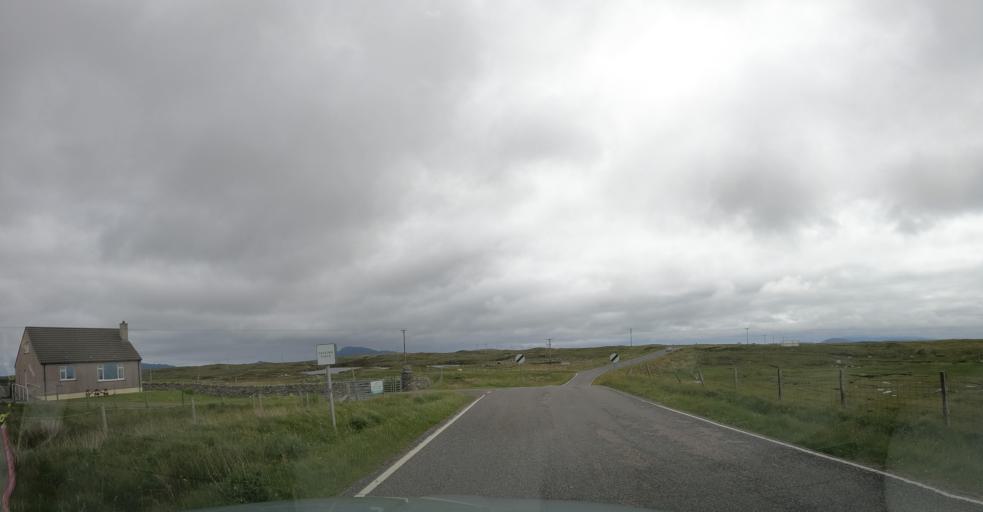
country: GB
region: Scotland
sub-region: Eilean Siar
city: Isle of North Uist
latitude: 57.5505
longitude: -7.3301
